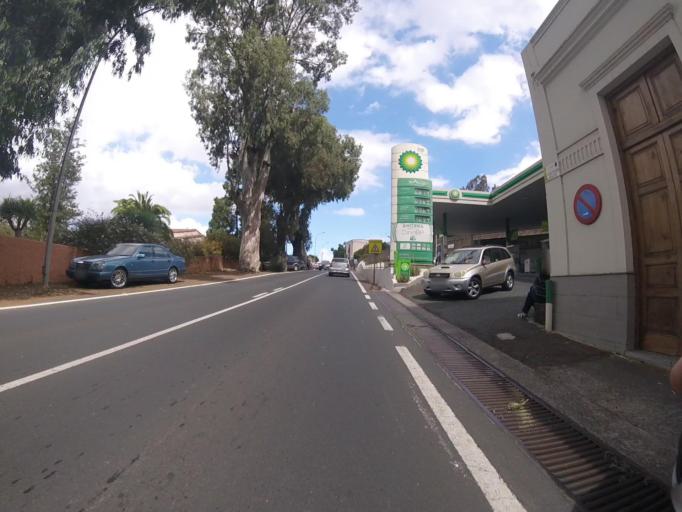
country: ES
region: Canary Islands
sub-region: Provincia de Las Palmas
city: Santa Brigida
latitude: 28.0303
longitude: -15.4998
